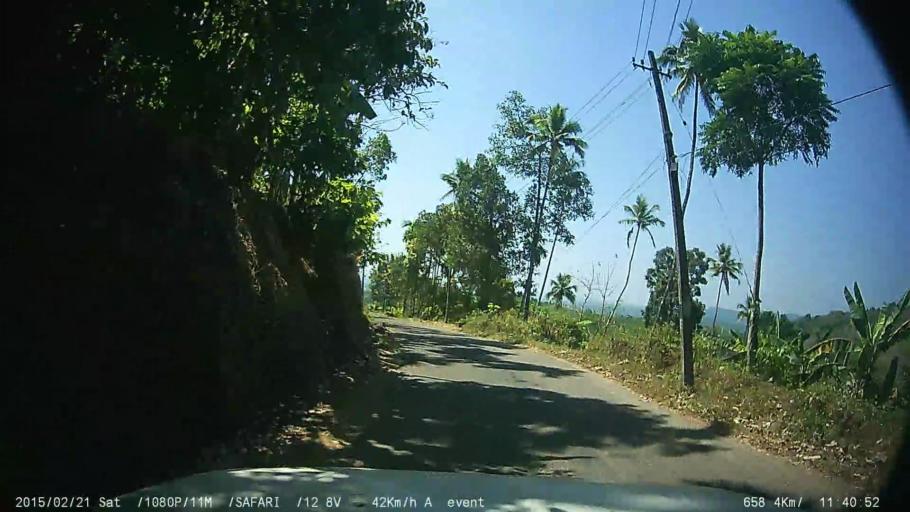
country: IN
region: Kerala
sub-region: Kottayam
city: Lalam
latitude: 9.7979
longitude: 76.7283
